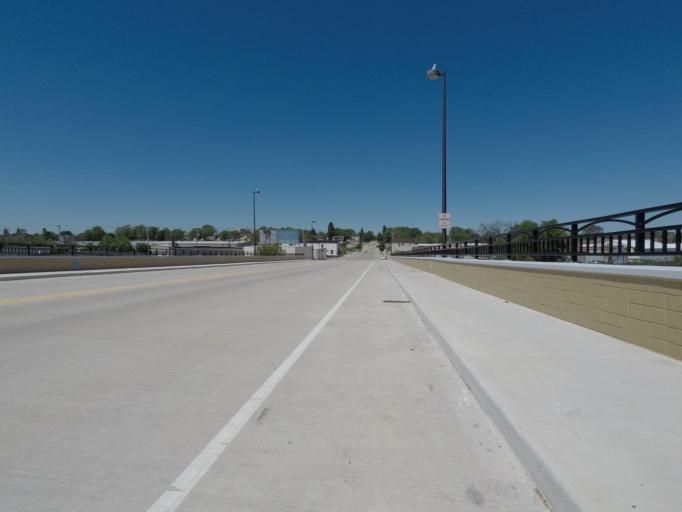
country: US
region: Wisconsin
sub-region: Sheboygan County
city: Sheboygan
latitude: 43.7499
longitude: -87.7167
